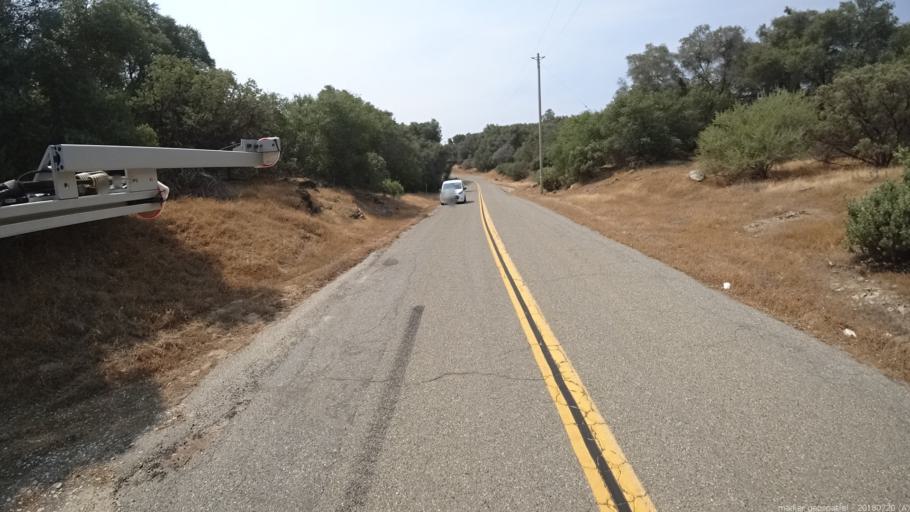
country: US
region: California
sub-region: Madera County
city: Ahwahnee
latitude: 37.3122
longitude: -119.7914
